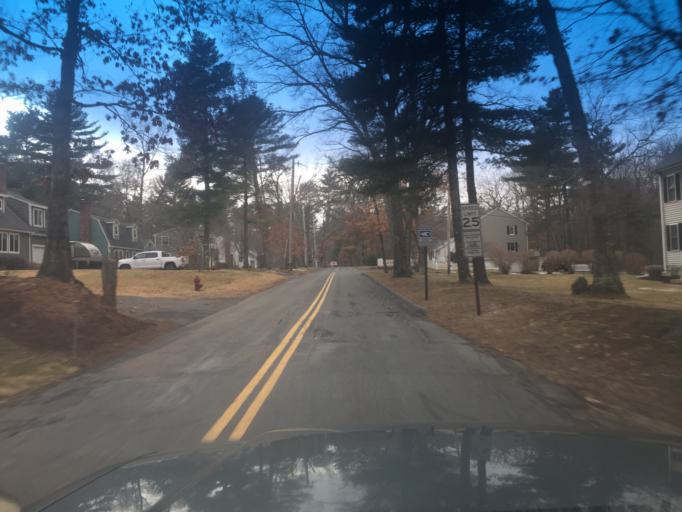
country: US
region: Massachusetts
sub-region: Norfolk County
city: Bellingham
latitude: 42.1174
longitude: -71.4439
